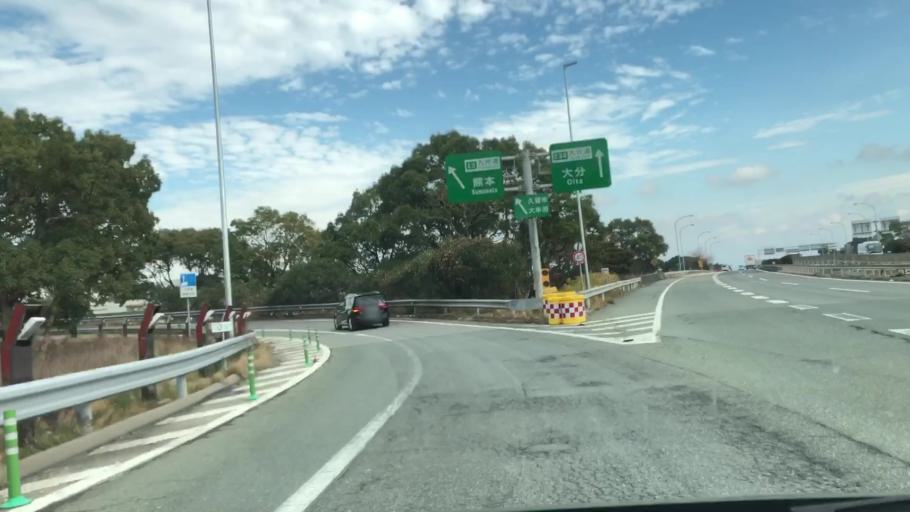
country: JP
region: Saga Prefecture
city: Tosu
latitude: 33.3969
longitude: 130.5394
